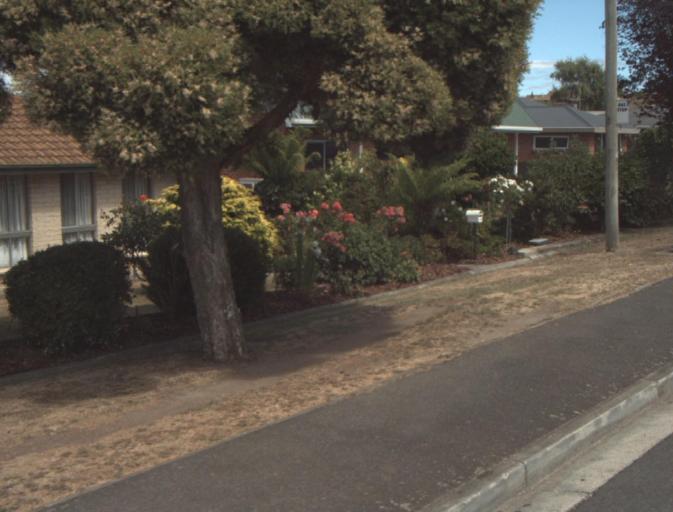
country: AU
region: Tasmania
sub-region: Launceston
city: Summerhill
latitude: -41.4630
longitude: 147.1337
